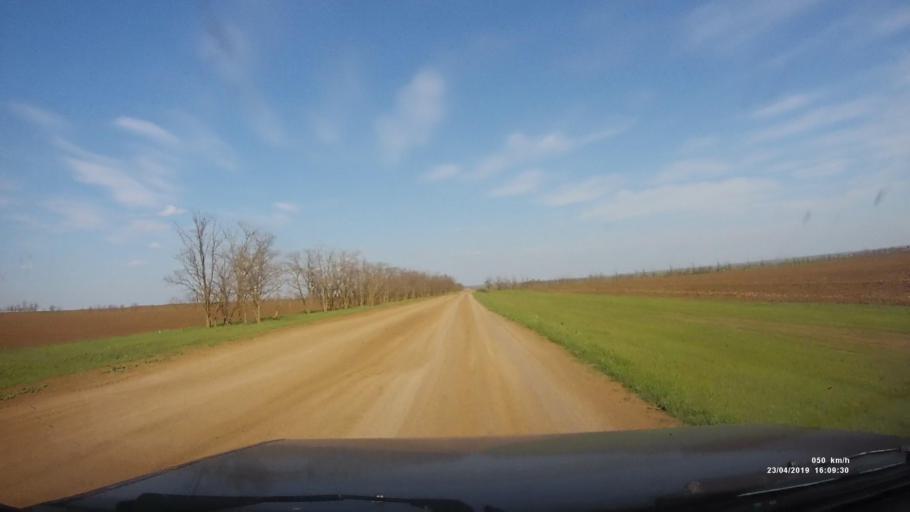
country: RU
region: Rostov
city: Remontnoye
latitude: 46.4818
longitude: 43.1111
